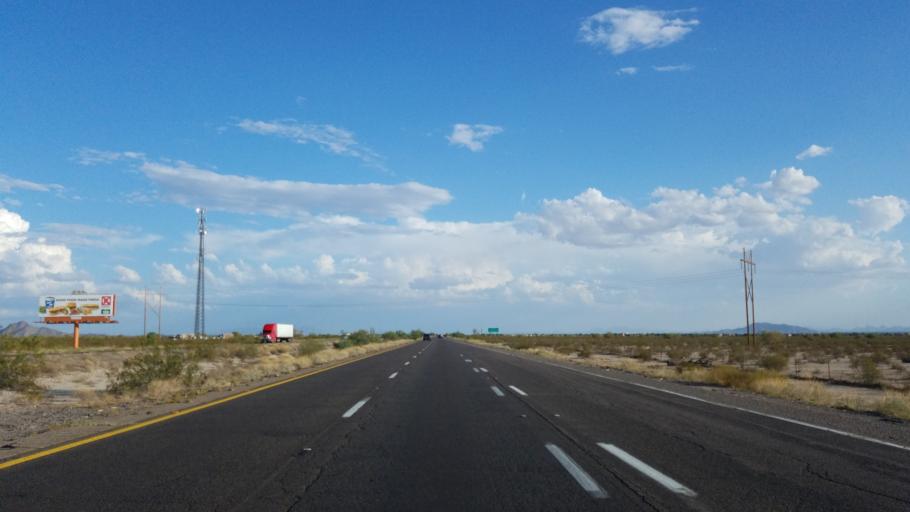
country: US
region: Arizona
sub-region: Pinal County
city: Sacaton
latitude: 32.9983
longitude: -111.7494
